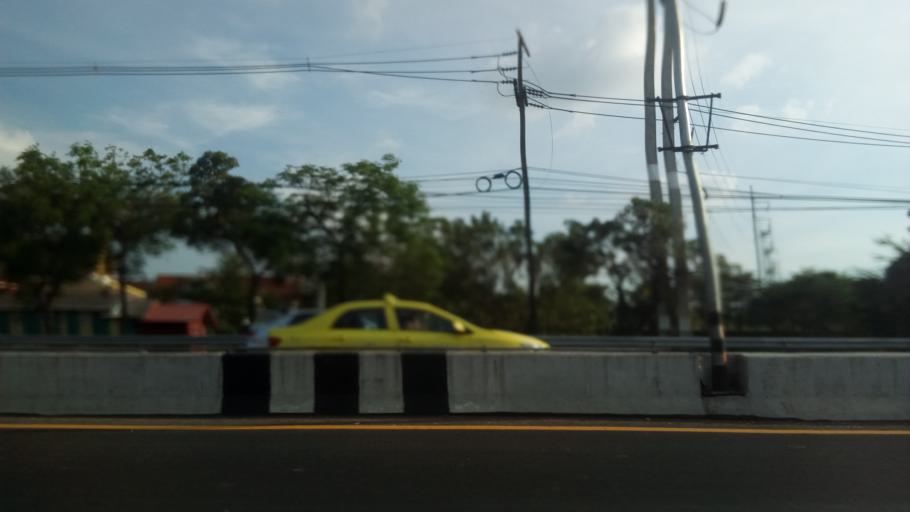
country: TH
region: Pathum Thani
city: Ban Rangsit
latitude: 14.0267
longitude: 100.7485
